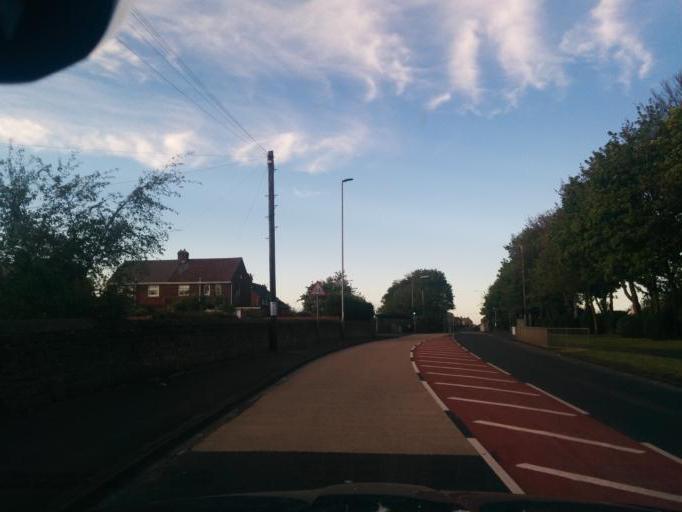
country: GB
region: England
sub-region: Northumberland
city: Newbiggin-by-the-Sea
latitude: 55.1775
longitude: -1.5231
